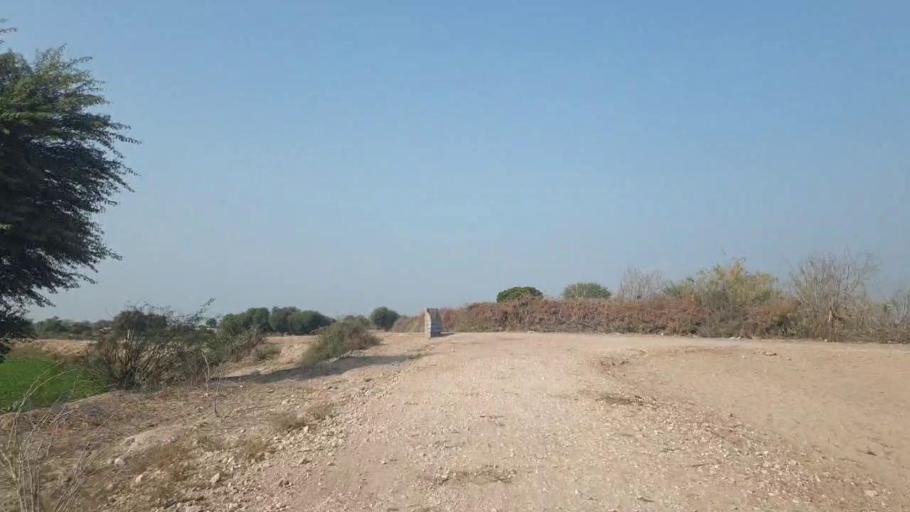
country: PK
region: Sindh
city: Hala
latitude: 25.8363
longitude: 68.4043
